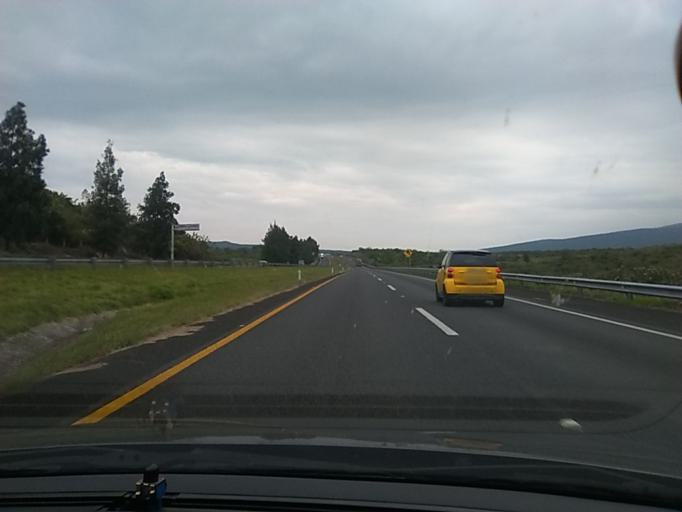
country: MX
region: Michoacan
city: Penjamillo de Degollado
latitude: 20.0376
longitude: -101.9315
